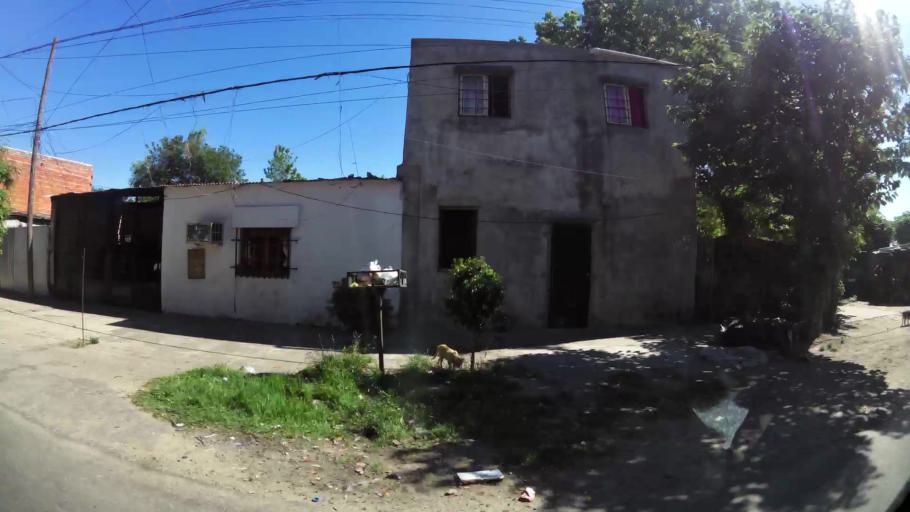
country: AR
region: Santa Fe
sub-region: Departamento de Rosario
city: Rosario
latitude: -32.9545
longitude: -60.6894
